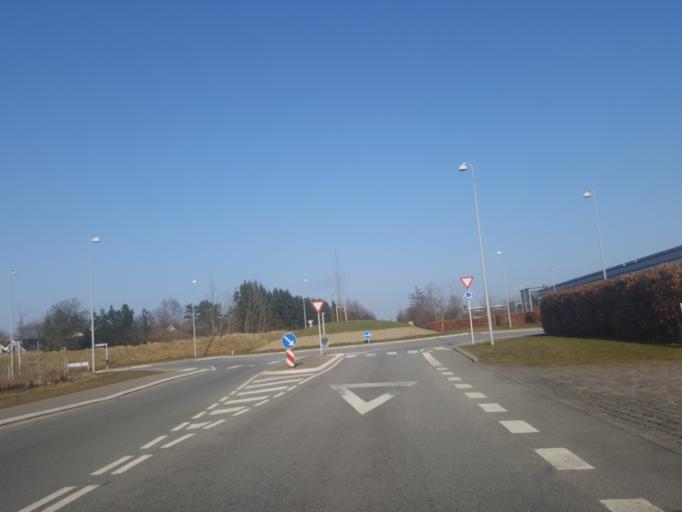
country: DK
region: Capital Region
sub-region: Allerod Kommune
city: Lillerod
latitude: 55.8660
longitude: 12.3237
